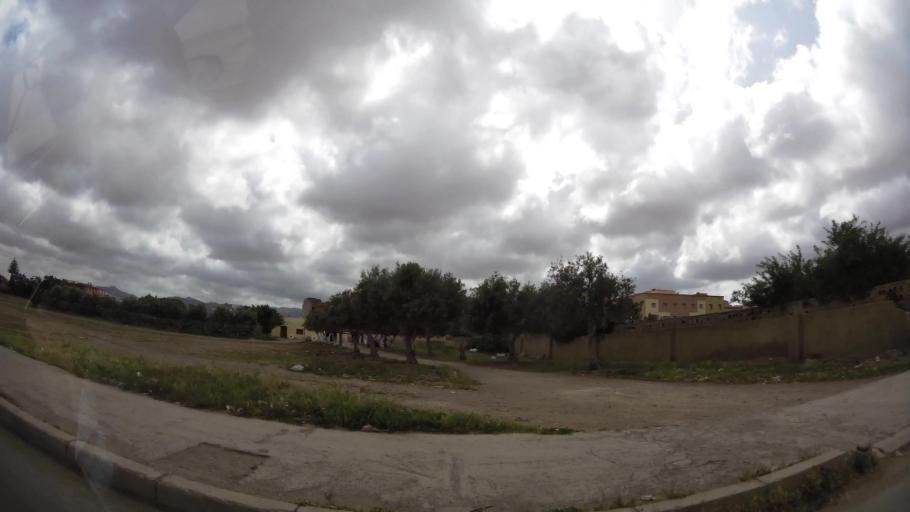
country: MA
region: Oriental
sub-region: Nador
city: Nador
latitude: 35.1645
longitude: -2.9413
